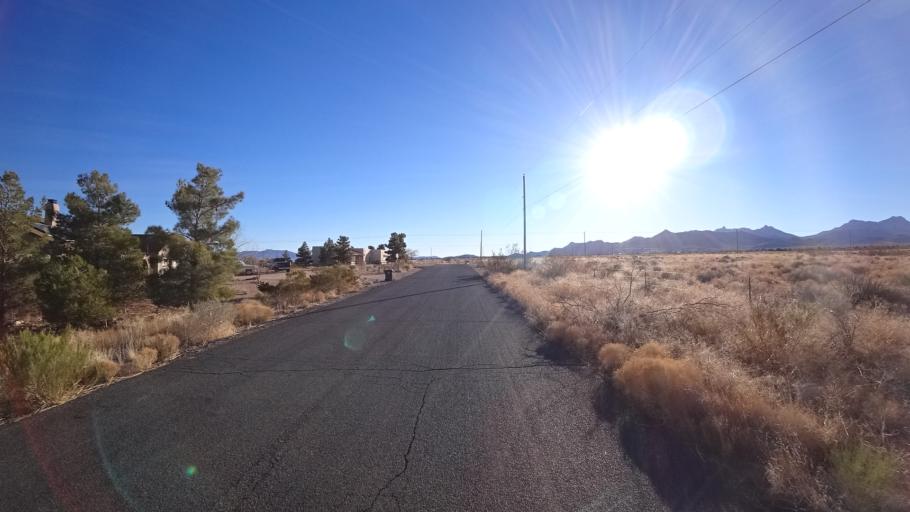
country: US
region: Arizona
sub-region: Mohave County
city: Kingman
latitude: 35.2031
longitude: -113.9954
